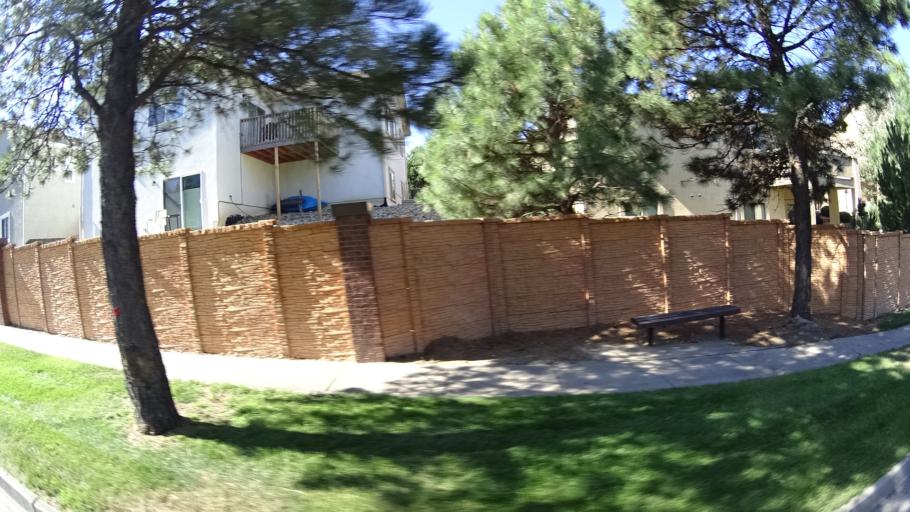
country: US
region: Colorado
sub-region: El Paso County
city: Cimarron Hills
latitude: 38.9224
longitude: -104.7451
